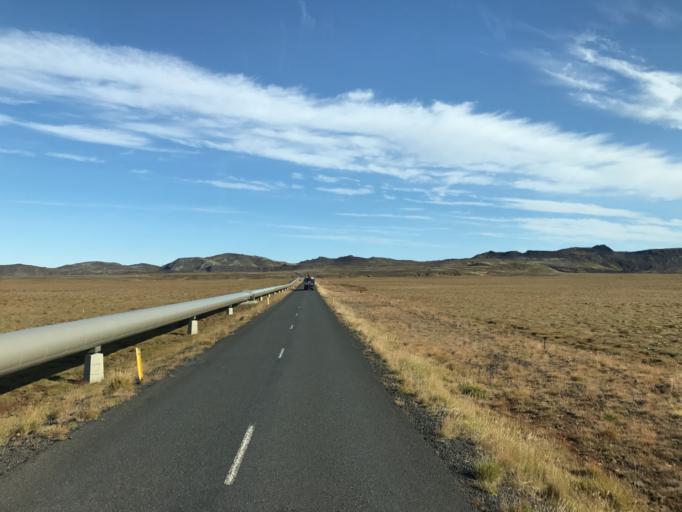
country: IS
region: South
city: Hveragerdi
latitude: 64.1228
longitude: -21.3742
